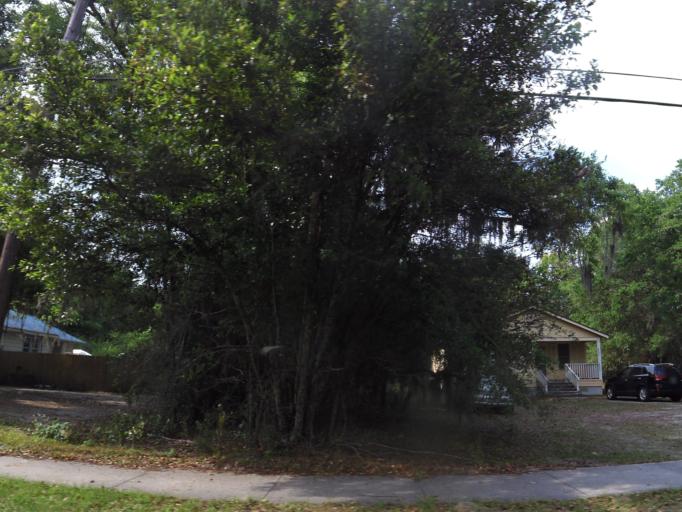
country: US
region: Georgia
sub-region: Charlton County
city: Folkston
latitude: 30.8335
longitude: -81.9951
